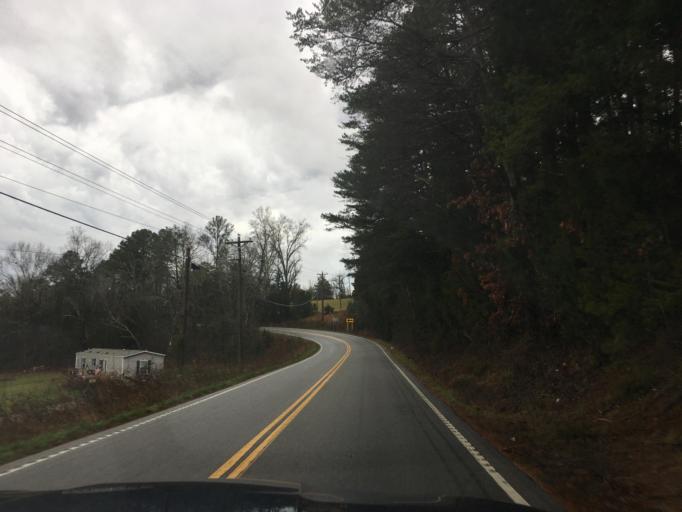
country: US
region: Tennessee
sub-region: McMinn County
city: Englewood
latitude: 35.3493
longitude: -84.3538
